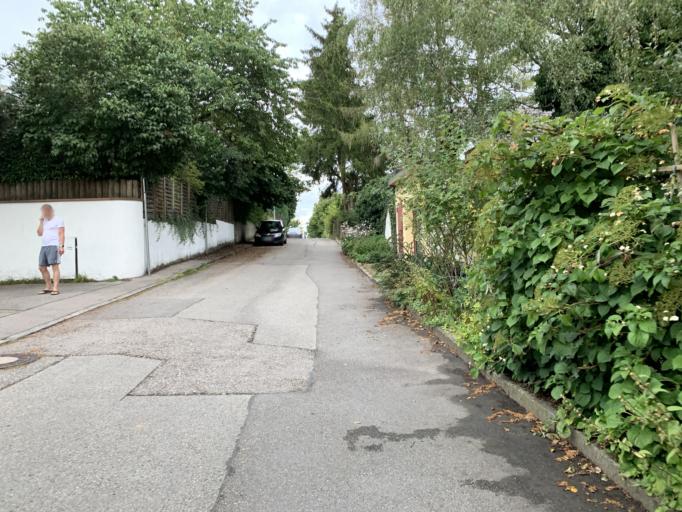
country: DE
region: Bavaria
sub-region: Upper Bavaria
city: Freising
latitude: 48.3964
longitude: 11.7132
